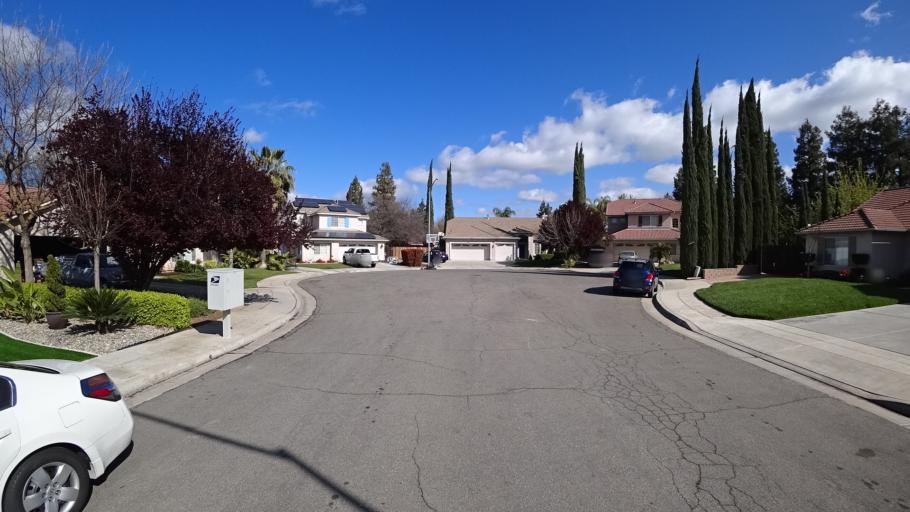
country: US
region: California
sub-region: Fresno County
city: West Park
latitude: 36.8304
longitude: -119.8880
